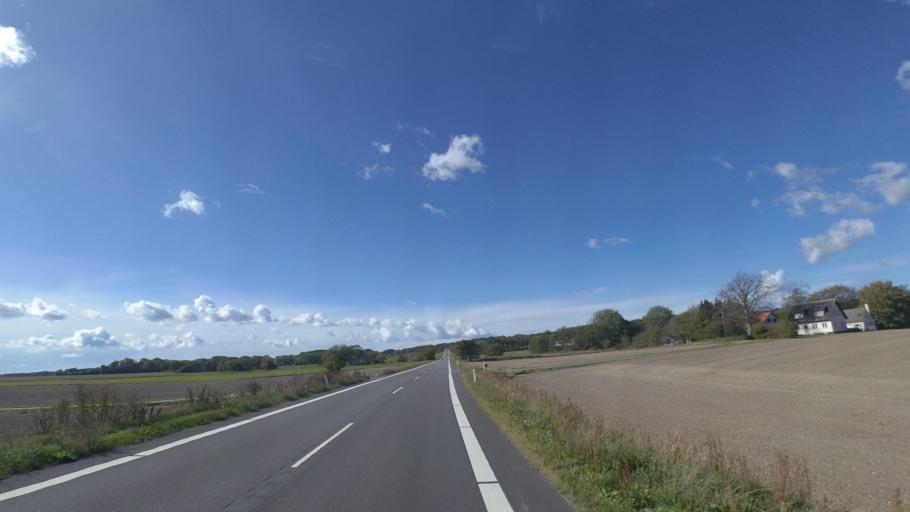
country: DK
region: Capital Region
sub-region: Bornholm Kommune
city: Nexo
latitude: 55.0607
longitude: 15.0476
